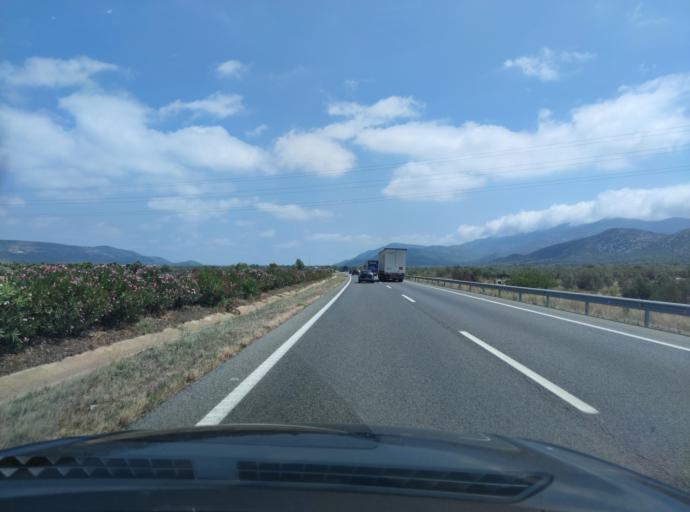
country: ES
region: Catalonia
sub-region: Provincia de Tarragona
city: Ulldecona
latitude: 40.5897
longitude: 0.4637
